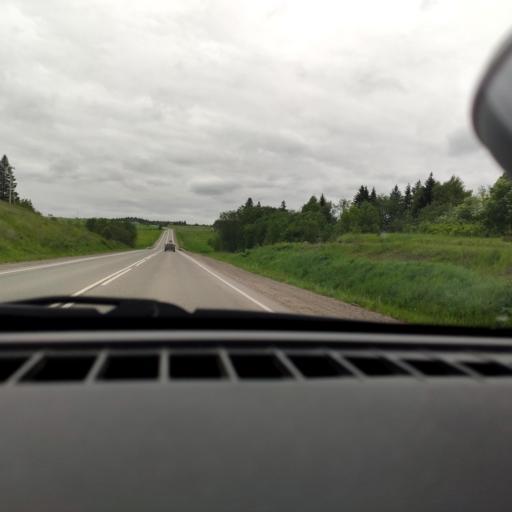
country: RU
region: Perm
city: Kultayevo
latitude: 57.8989
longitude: 55.7873
